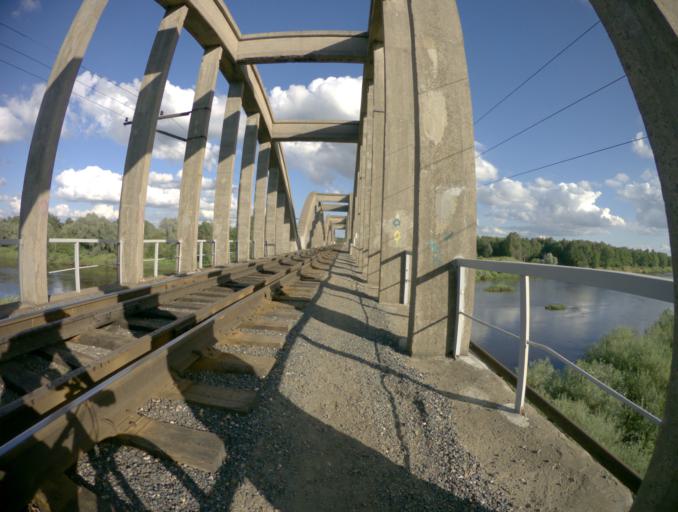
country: RU
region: Vladimir
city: Raduzhnyy
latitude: 56.0541
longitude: 40.3732
